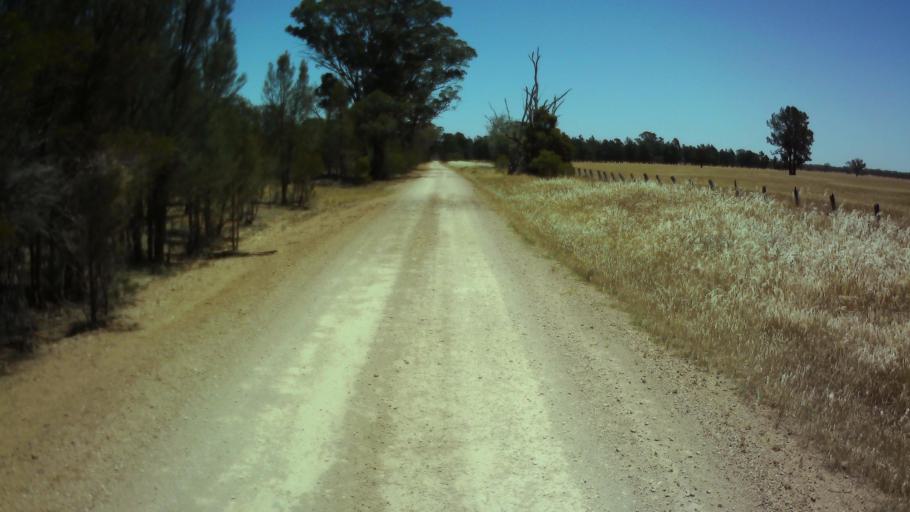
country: AU
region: New South Wales
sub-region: Weddin
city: Grenfell
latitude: -33.9908
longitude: 147.9453
